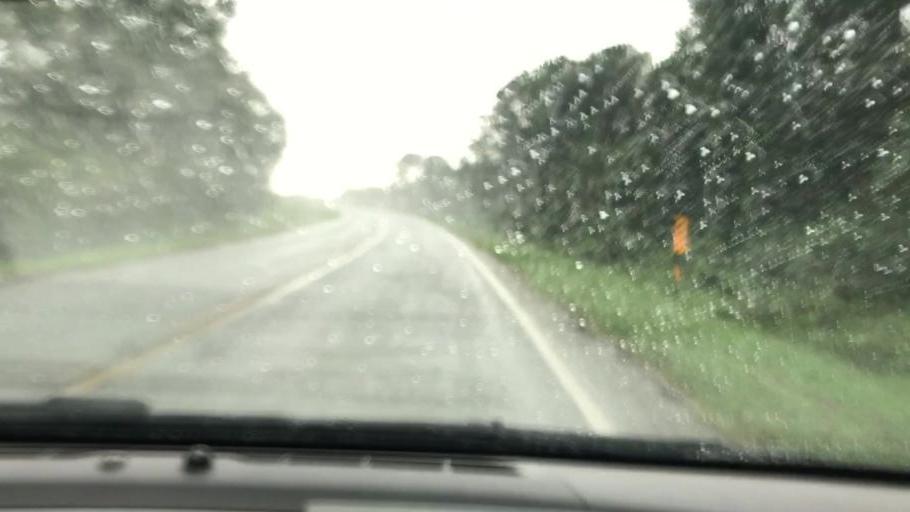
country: US
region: Georgia
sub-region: Clay County
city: Fort Gaines
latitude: 31.6669
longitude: -85.0470
